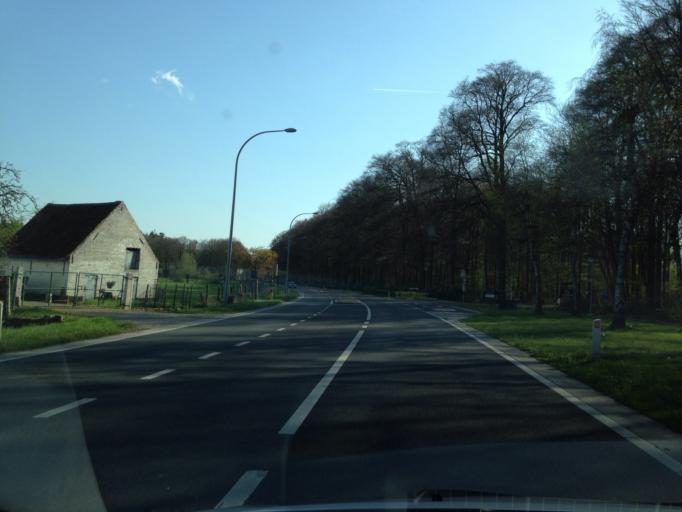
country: BE
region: Flanders
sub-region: Provincie West-Vlaanderen
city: Zedelgem
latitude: 51.1611
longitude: 3.1672
